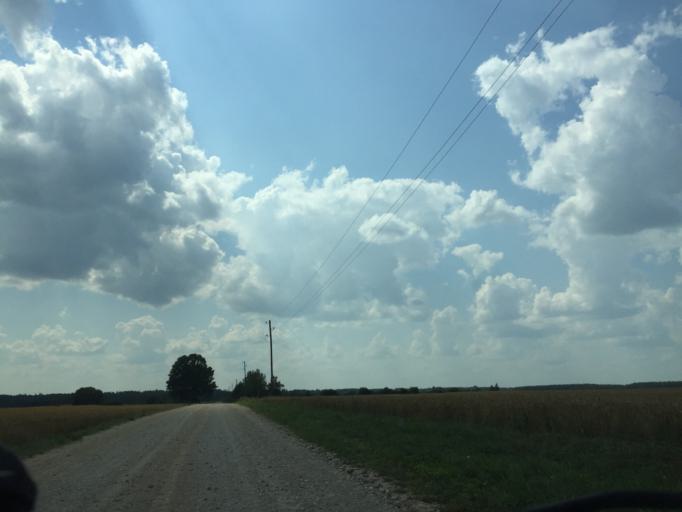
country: LT
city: Zagare
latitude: 56.3846
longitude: 23.1830
